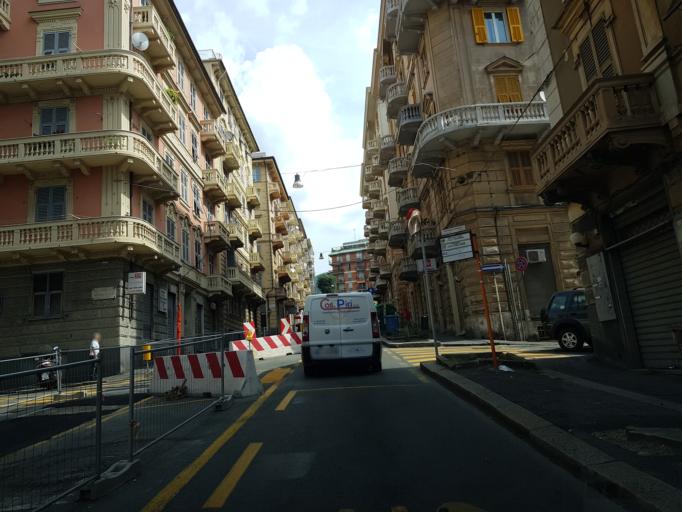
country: IT
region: Liguria
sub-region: Provincia di Genova
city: San Teodoro
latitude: 44.4276
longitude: 8.8511
